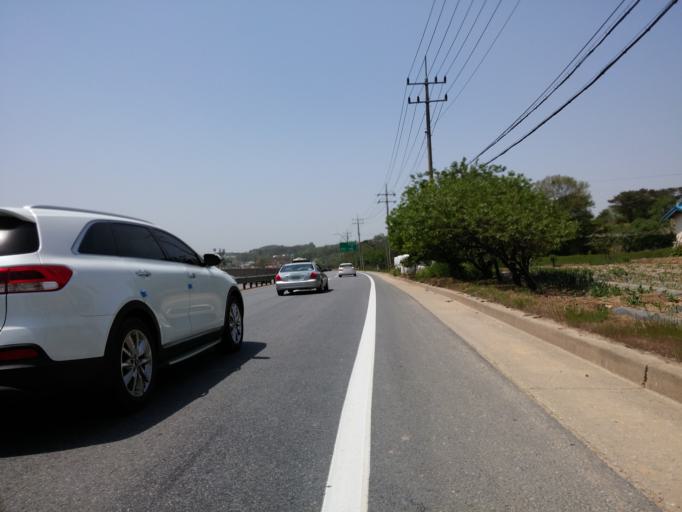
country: KR
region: Chungcheongnam-do
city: Nonsan
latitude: 36.2144
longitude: 127.1655
